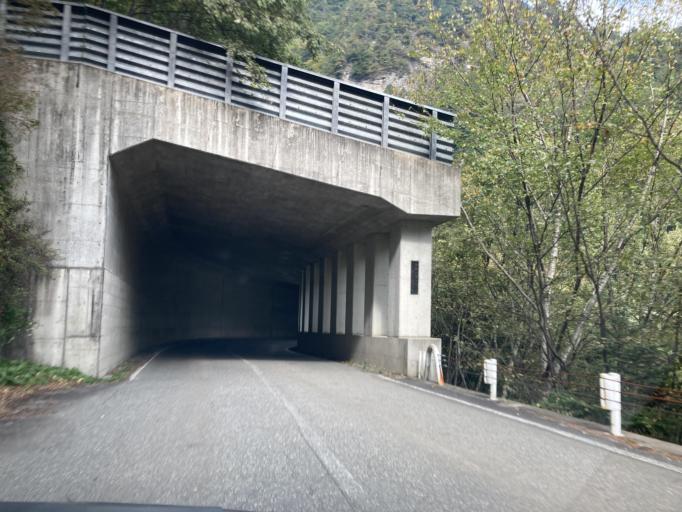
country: JP
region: Nagano
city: Omachi
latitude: 36.4924
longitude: 137.7403
